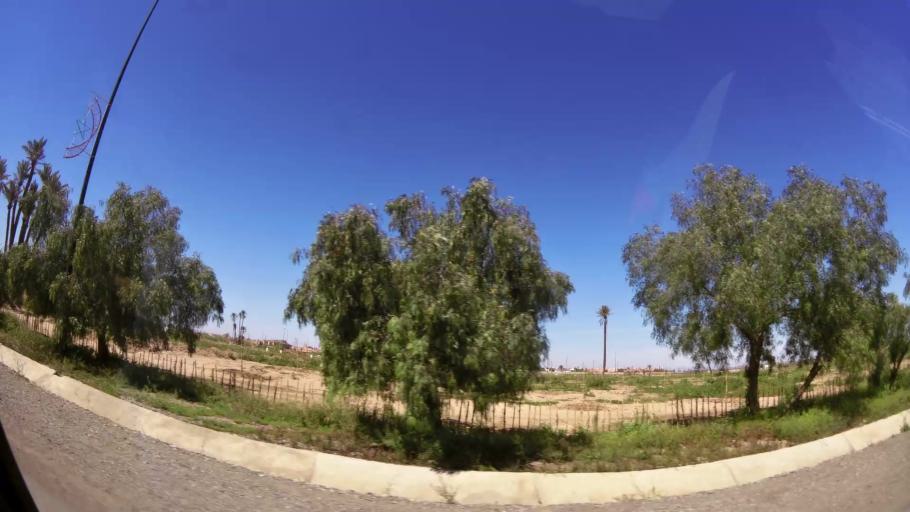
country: MA
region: Marrakech-Tensift-Al Haouz
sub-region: Marrakech
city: Marrakesh
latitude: 31.6778
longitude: -7.9915
